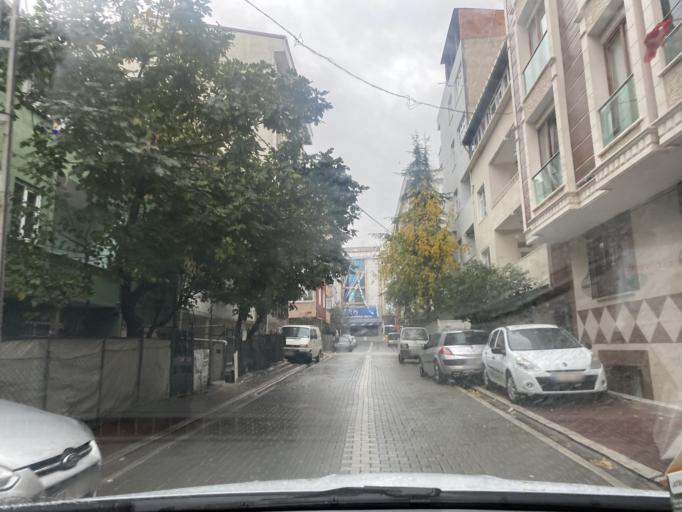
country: TR
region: Istanbul
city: Esenyurt
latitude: 41.0202
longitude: 28.6659
